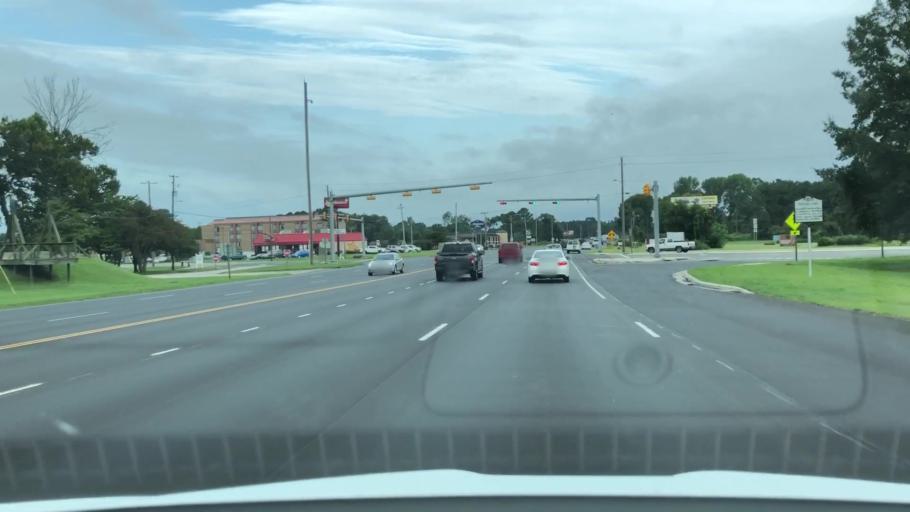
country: US
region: North Carolina
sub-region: Lenoir County
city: Kinston
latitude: 35.2442
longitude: -77.5841
